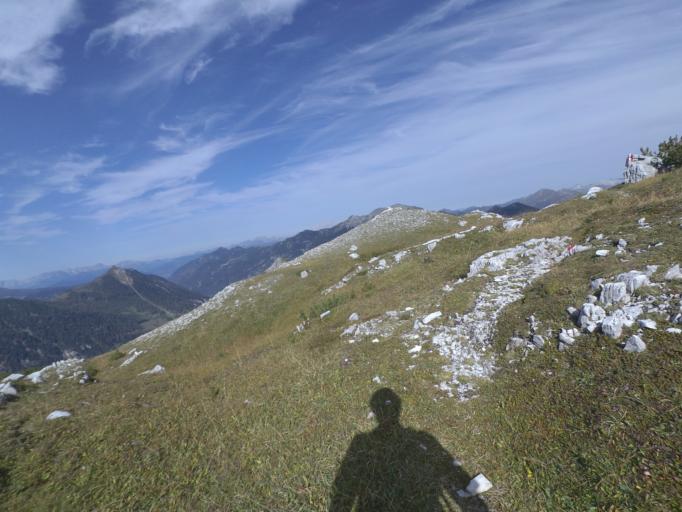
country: AT
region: Salzburg
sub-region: Politischer Bezirk Sankt Johann im Pongau
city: Kleinarl
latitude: 47.2285
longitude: 13.4026
